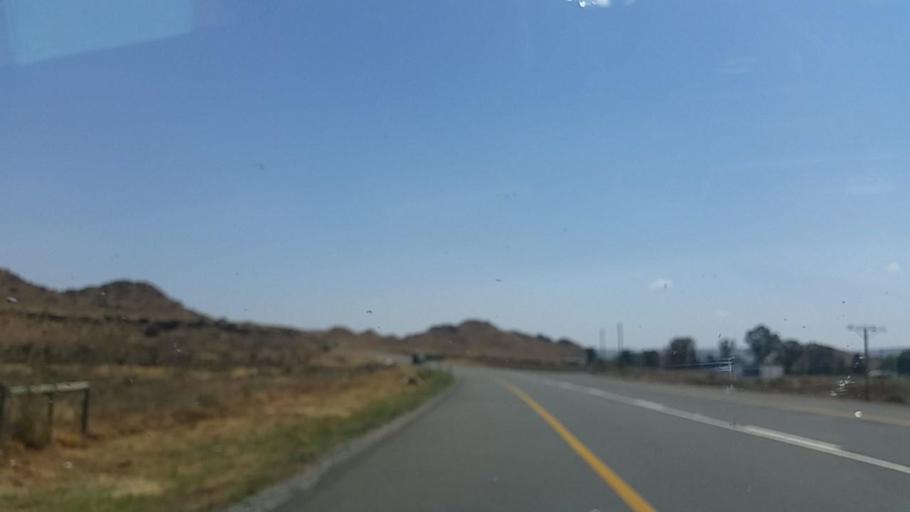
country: ZA
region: Eastern Cape
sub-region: Chris Hani District Municipality
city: Middelburg
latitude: -31.3618
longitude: 25.0167
